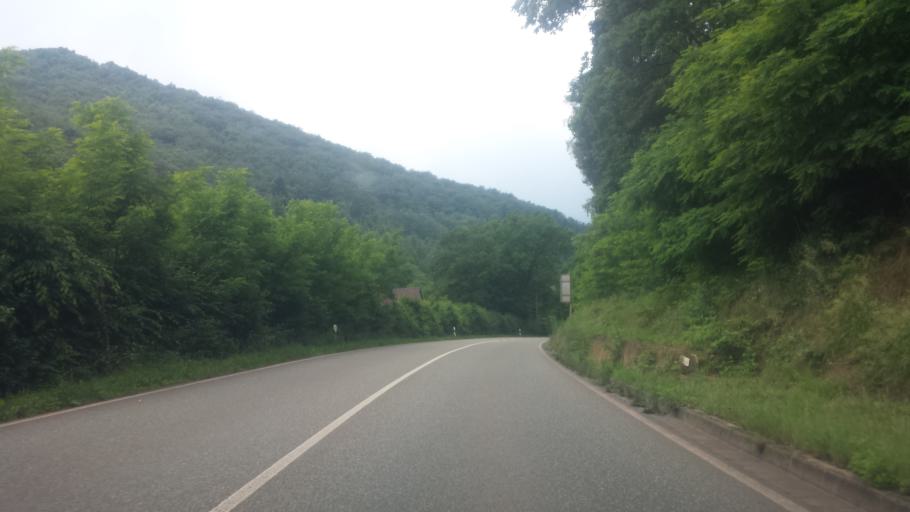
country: DE
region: Rheinland-Pfalz
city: Klingenmunster
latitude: 49.1570
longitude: 8.0104
